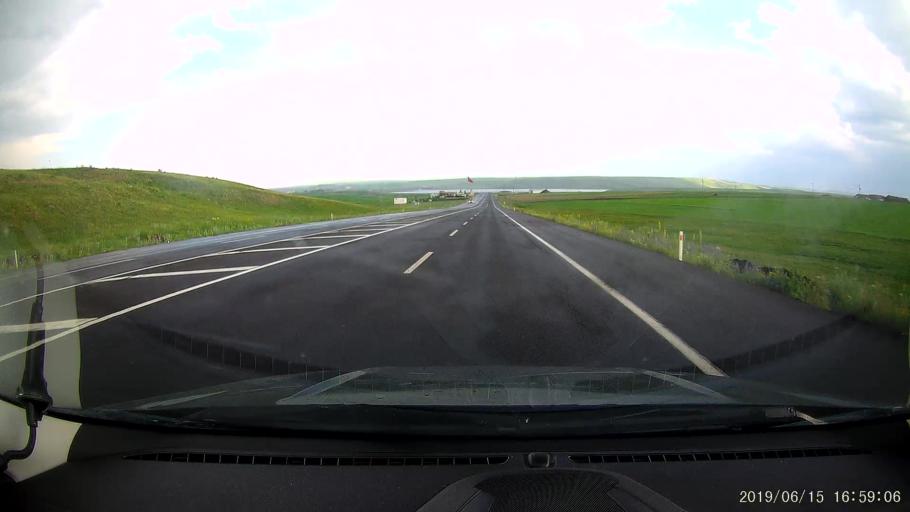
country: TR
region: Kars
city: Susuz
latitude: 40.7568
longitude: 43.1481
